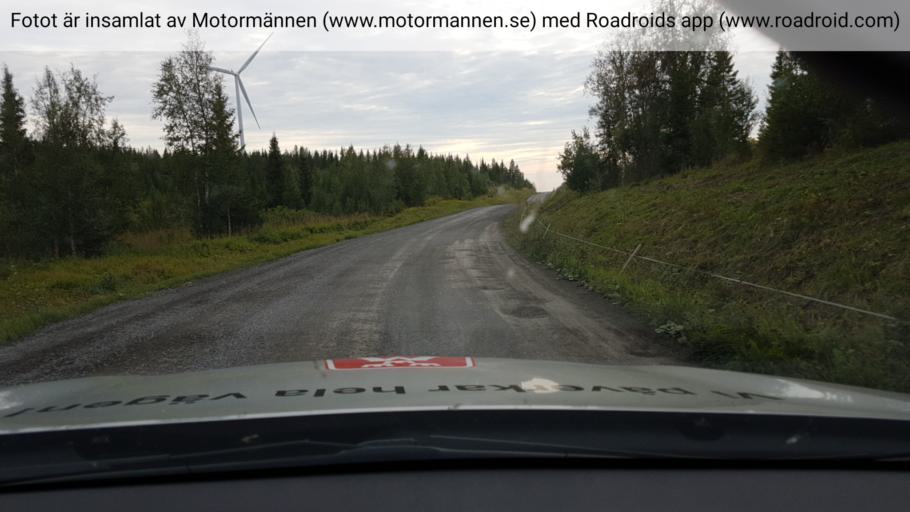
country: SE
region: Jaemtland
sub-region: OEstersunds Kommun
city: Lit
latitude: 63.6005
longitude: 14.9968
